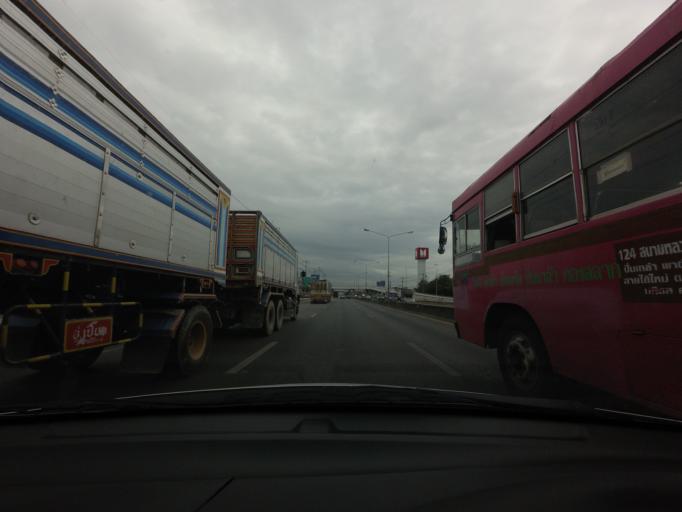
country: TH
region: Nakhon Pathom
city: Salaya
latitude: 13.7862
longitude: 100.2852
